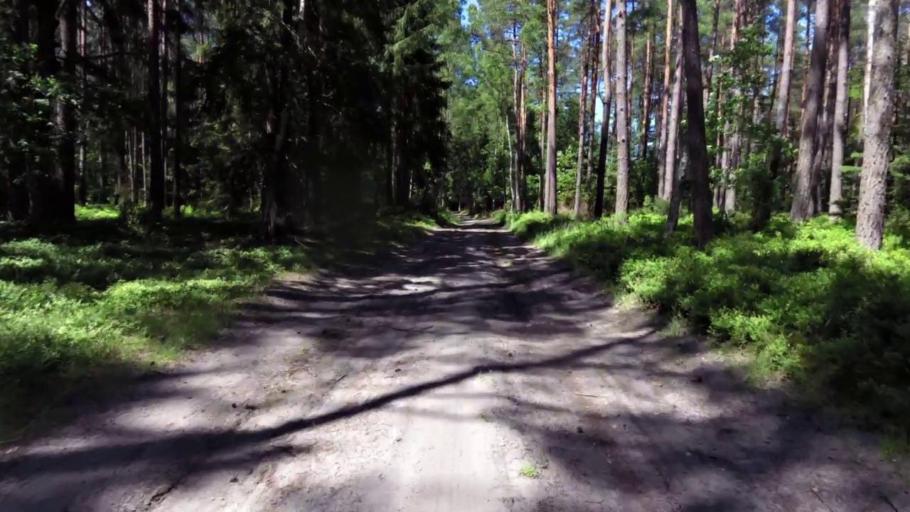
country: PL
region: West Pomeranian Voivodeship
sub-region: Powiat bialogardzki
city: Bialogard
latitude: 53.9554
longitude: 16.0982
